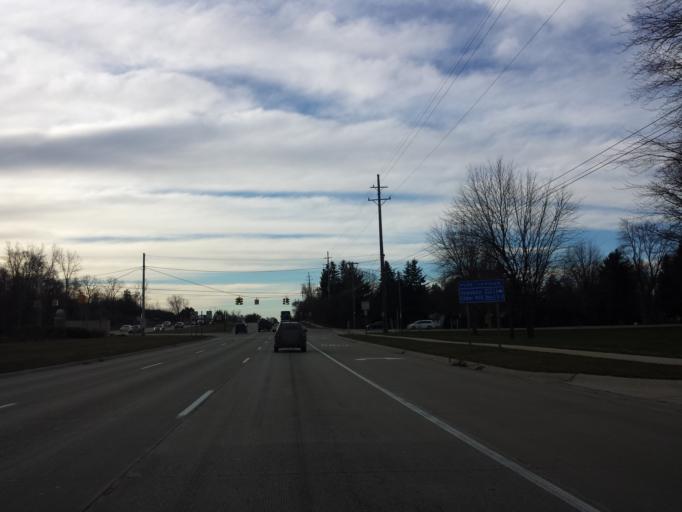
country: US
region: Michigan
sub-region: Oakland County
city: Bingham Farms
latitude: 42.5310
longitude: -83.2853
